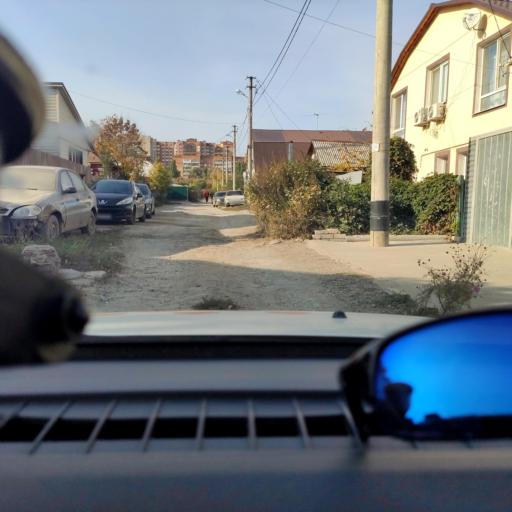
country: RU
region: Samara
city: Samara
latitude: 53.2296
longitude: 50.2301
